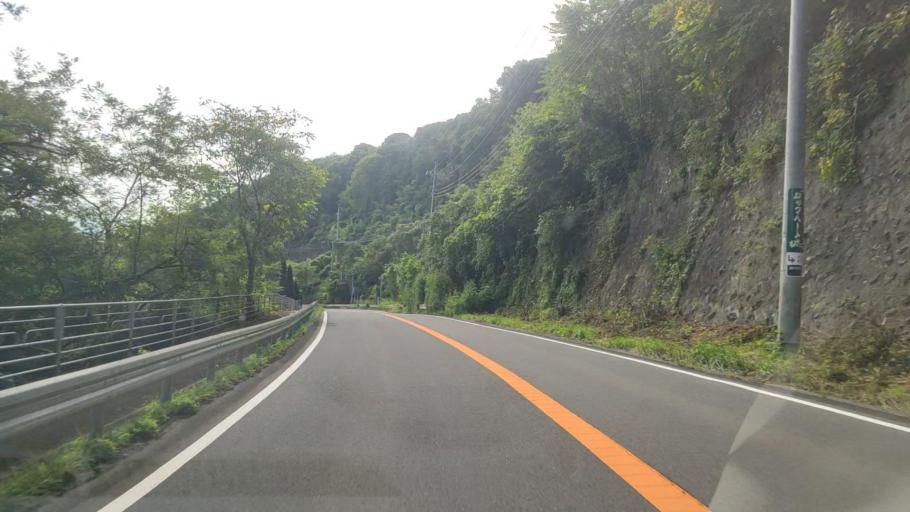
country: JP
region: Gunma
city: Numata
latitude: 36.6246
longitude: 139.0352
